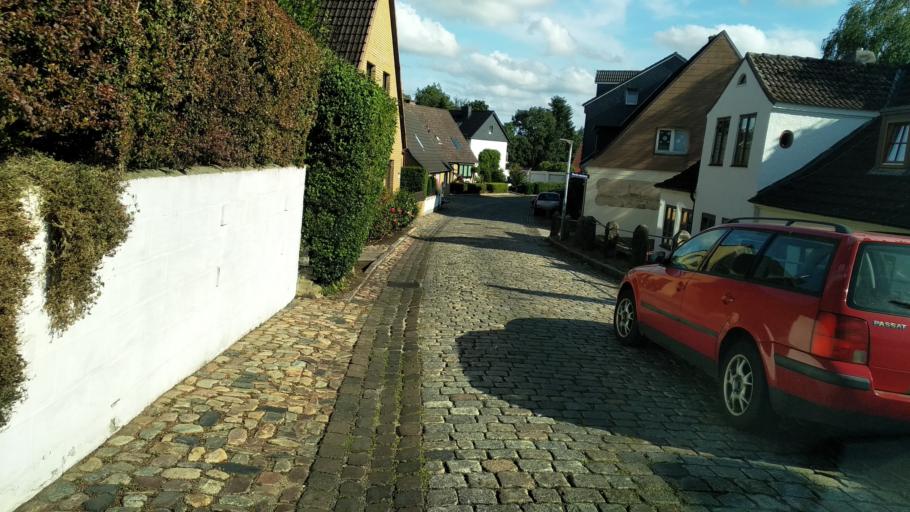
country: DE
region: Schleswig-Holstein
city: Schleswig
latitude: 54.5159
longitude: 9.5477
